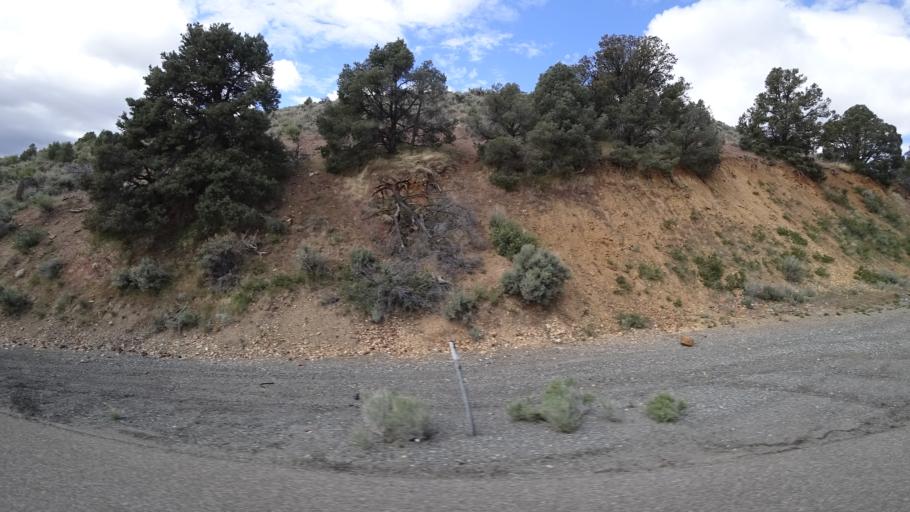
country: US
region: Nevada
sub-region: Lyon County
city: Smith Valley
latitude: 38.7074
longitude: -119.5527
